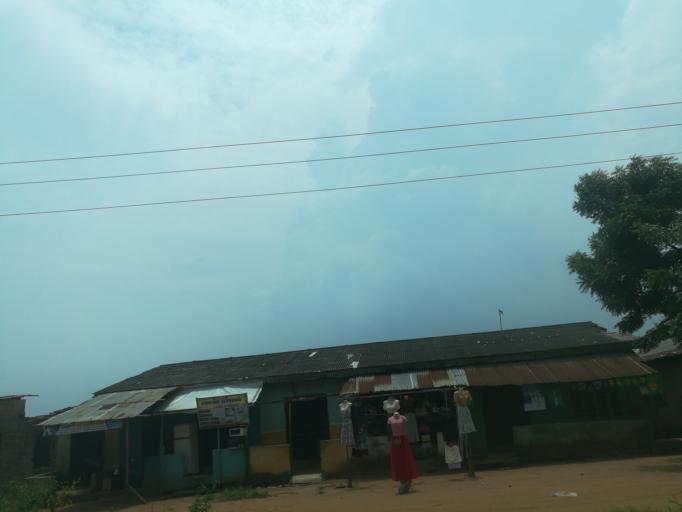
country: NG
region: Lagos
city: Ikorodu
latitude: 6.6024
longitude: 3.5874
